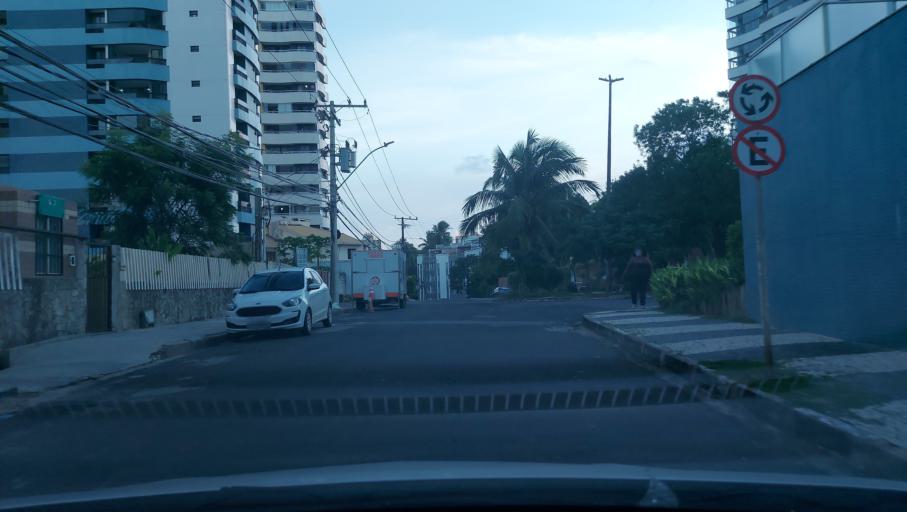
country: BR
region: Bahia
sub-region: Salvador
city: Salvador
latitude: -12.9877
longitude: -38.4393
